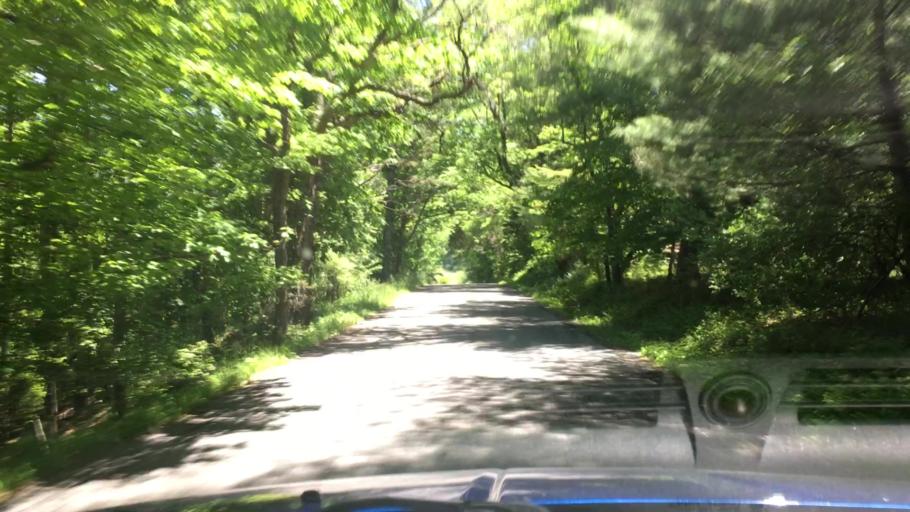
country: US
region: Virginia
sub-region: Bath County
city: Warm Springs
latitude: 38.0746
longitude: -79.5852
